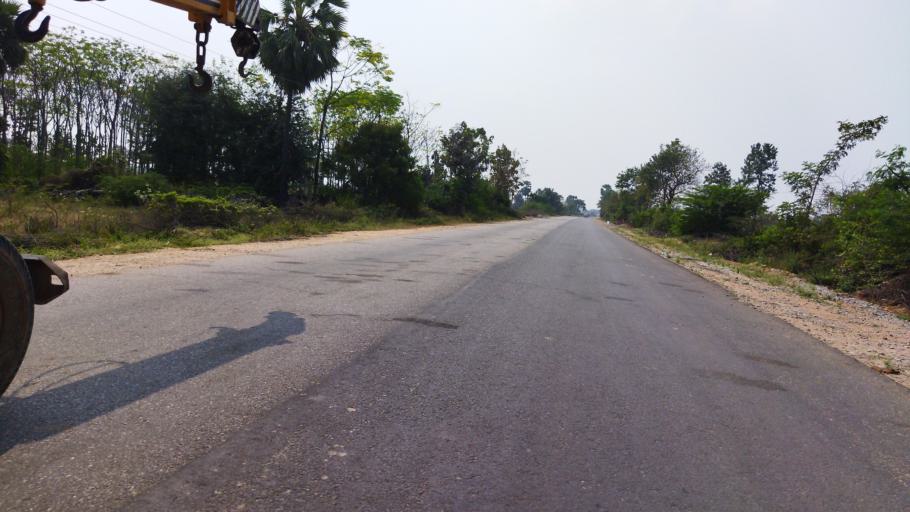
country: IN
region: Telangana
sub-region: Nalgonda
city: Nalgonda
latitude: 17.0991
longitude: 79.3397
